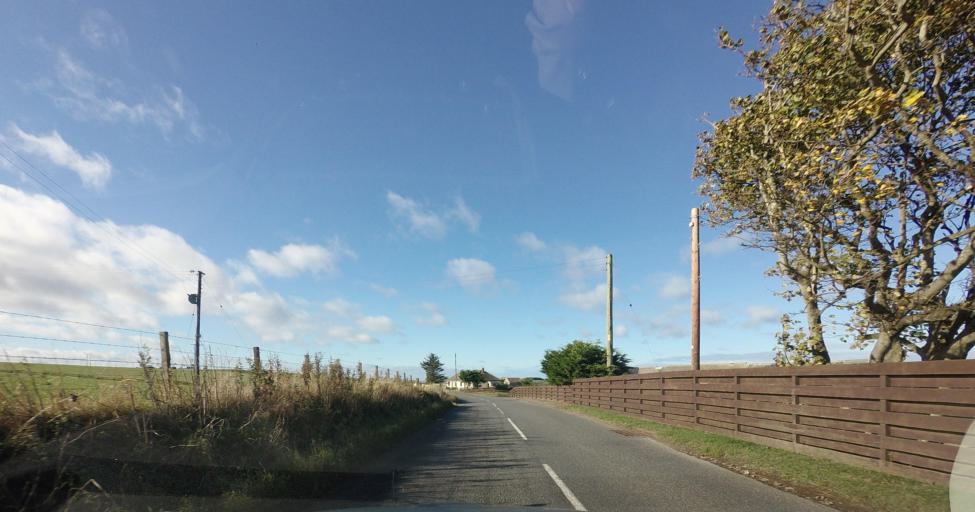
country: GB
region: Scotland
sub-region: Aberdeenshire
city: Macduff
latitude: 57.6640
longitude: -2.3853
